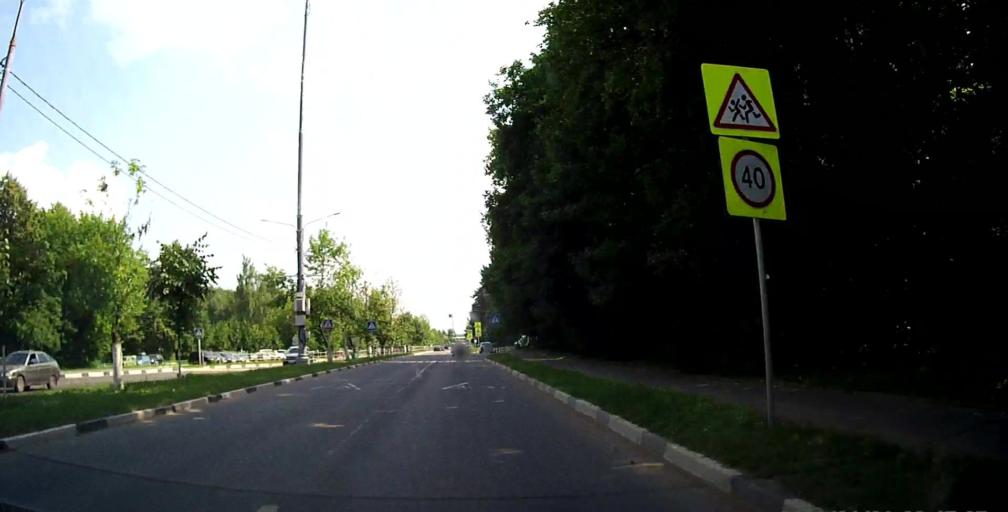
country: RU
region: Moskovskaya
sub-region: Podol'skiy Rayon
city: Podol'sk
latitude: 55.4155
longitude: 37.5213
